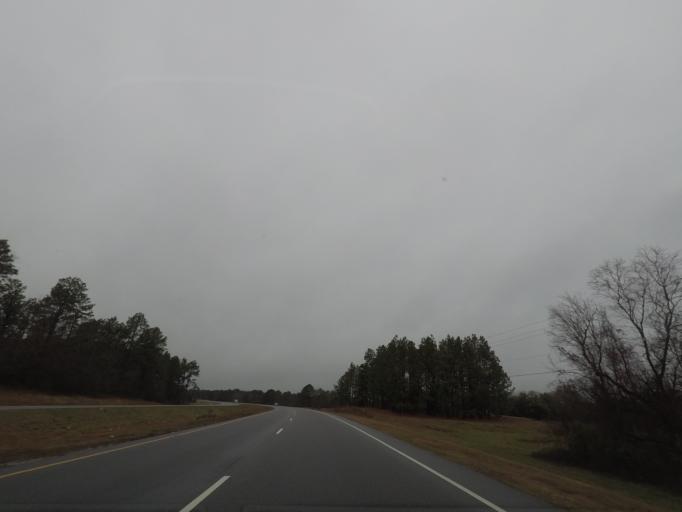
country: US
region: North Carolina
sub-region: Lee County
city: Broadway
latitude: 35.3343
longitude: -79.0948
